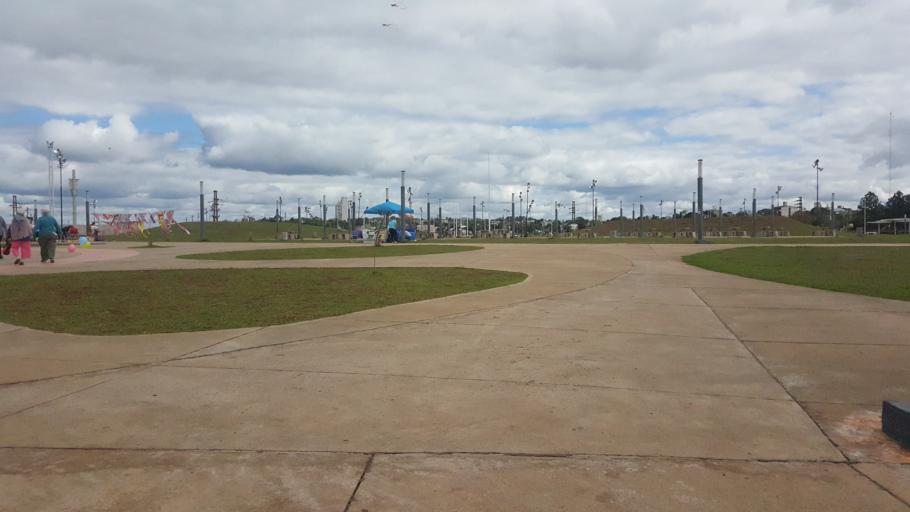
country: AR
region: Misiones
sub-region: Departamento de Capital
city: Posadas
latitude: -27.3740
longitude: -55.8837
